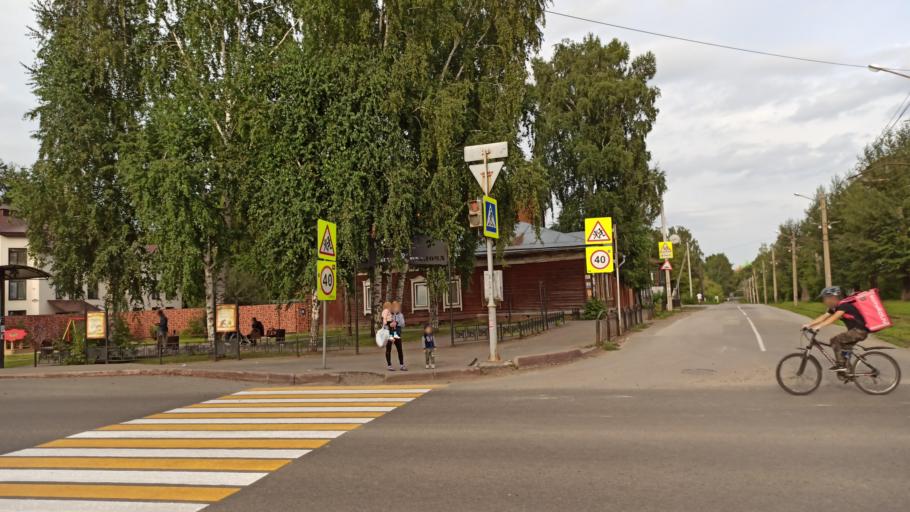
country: RU
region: Tomsk
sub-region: Tomskiy Rayon
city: Tomsk
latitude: 56.4793
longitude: 84.9549
